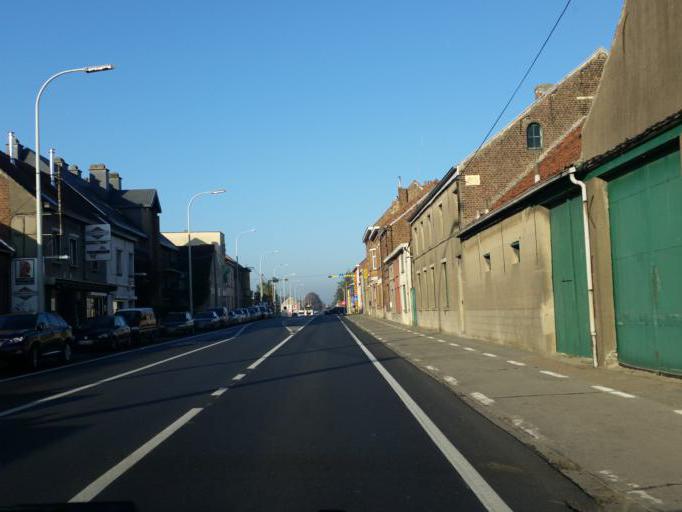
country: BE
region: Flanders
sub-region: Provincie Vlaams-Brabant
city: Asse
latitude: 50.8978
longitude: 4.2311
